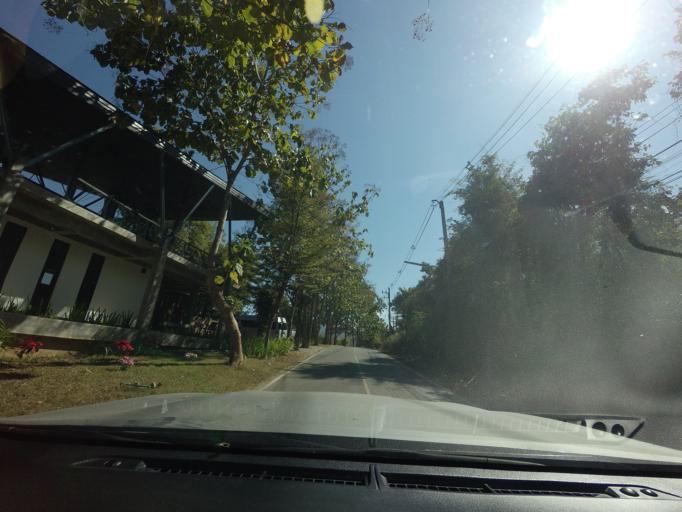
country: TH
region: Mae Hong Son
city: Wiang Nuea
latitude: 19.3872
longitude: 98.4344
